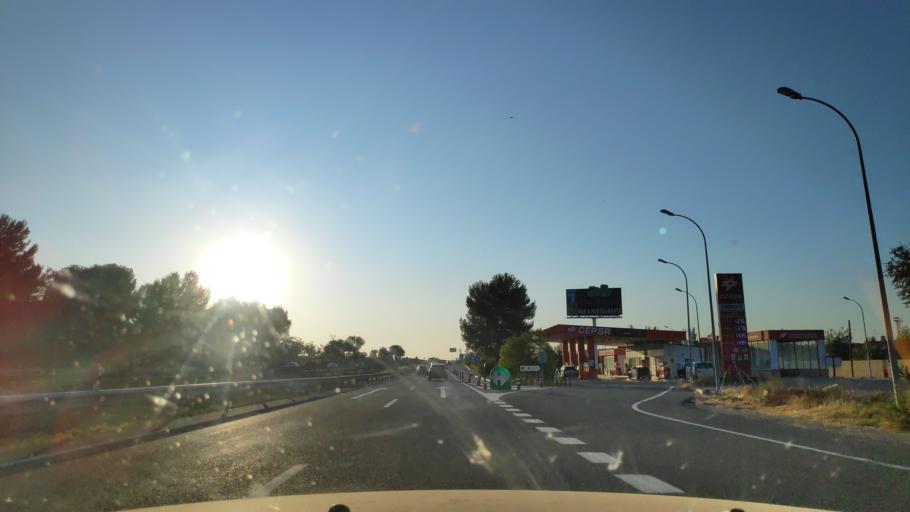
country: ES
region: Madrid
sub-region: Provincia de Madrid
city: Villarejo de Salvanes
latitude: 40.1671
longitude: -3.2847
